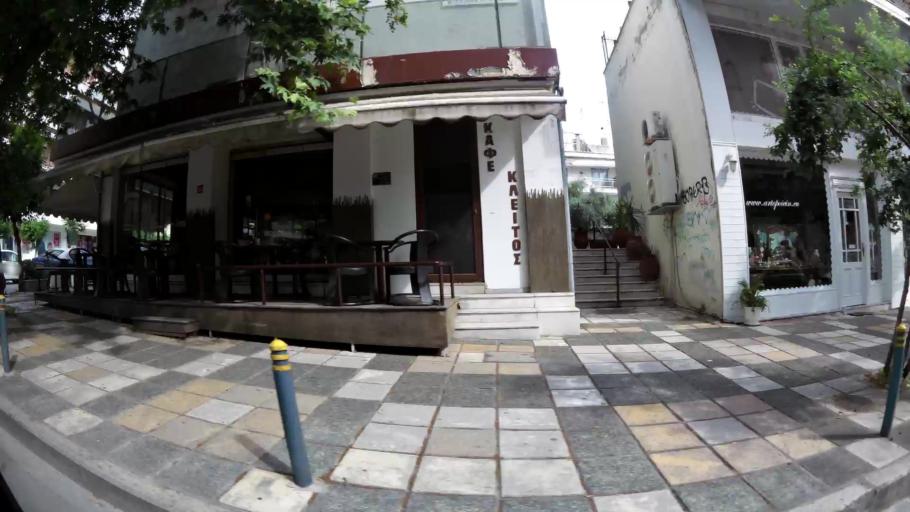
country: GR
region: Central Macedonia
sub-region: Nomos Thessalonikis
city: Kalamaria
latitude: 40.5790
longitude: 22.9477
